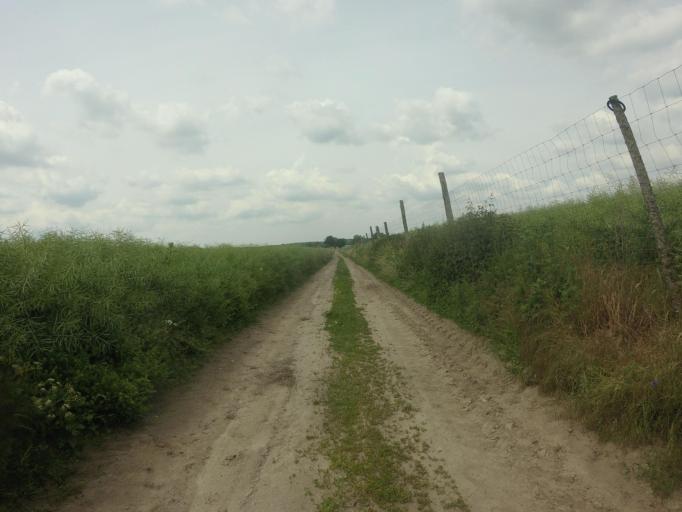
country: PL
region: West Pomeranian Voivodeship
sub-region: Powiat choszczenski
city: Recz
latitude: 53.2968
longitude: 15.4904
